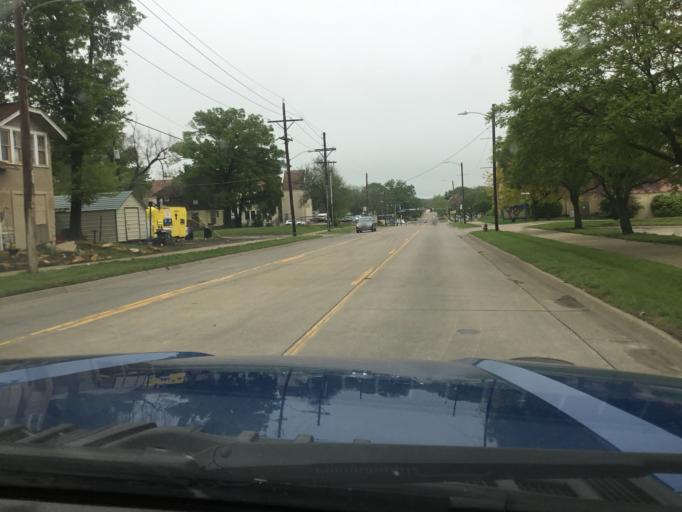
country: US
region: Kansas
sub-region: Shawnee County
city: Topeka
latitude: 39.0369
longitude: -95.6860
